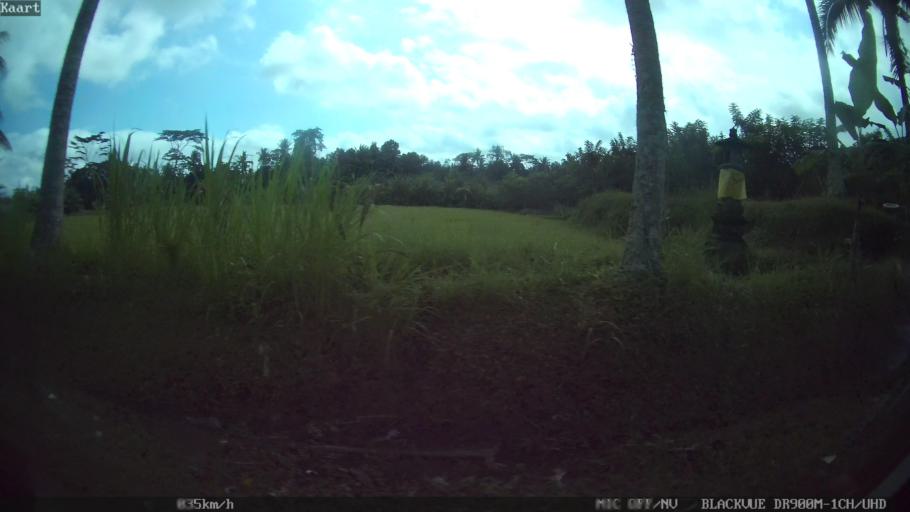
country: ID
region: Bali
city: Banjar Pesalakan
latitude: -8.5008
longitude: 115.3043
